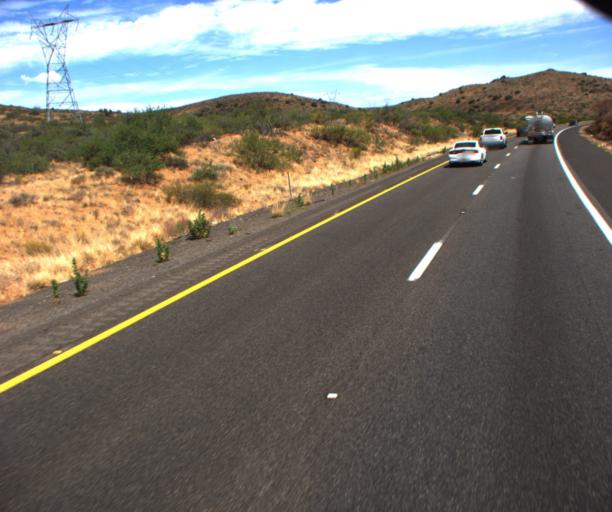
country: US
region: Arizona
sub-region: Yavapai County
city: Cordes Lakes
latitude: 34.2992
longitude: -112.1268
